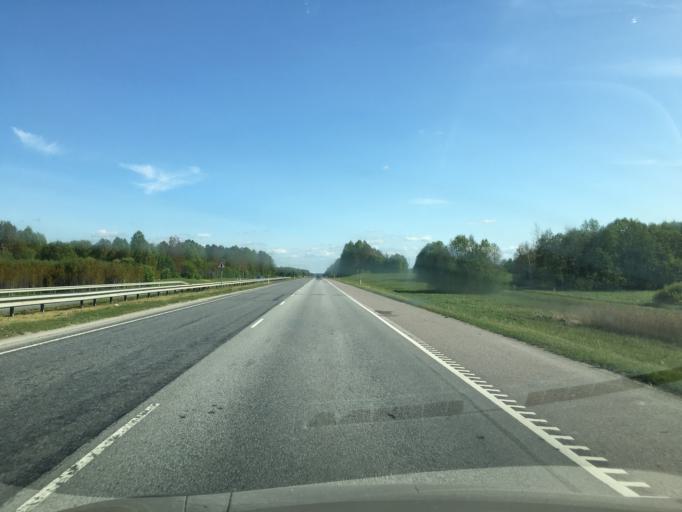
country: EE
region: Harju
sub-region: Rae vald
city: Jueri
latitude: 59.3360
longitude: 24.9074
